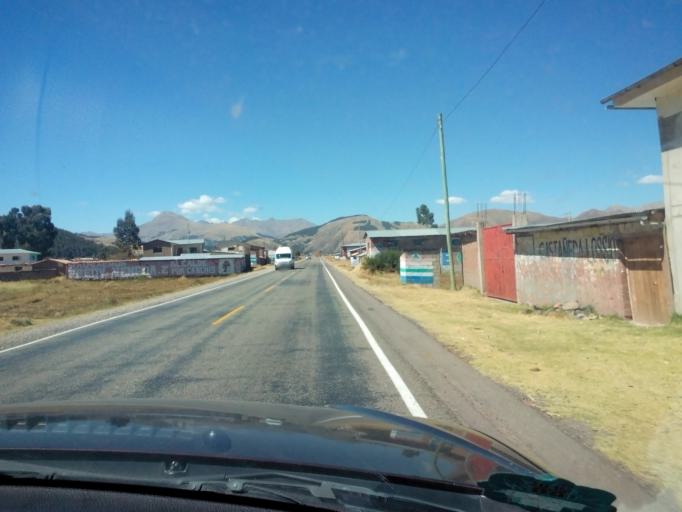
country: PE
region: Cusco
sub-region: Provincia de Canchis
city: San Pablo
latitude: -14.2209
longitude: -71.2887
